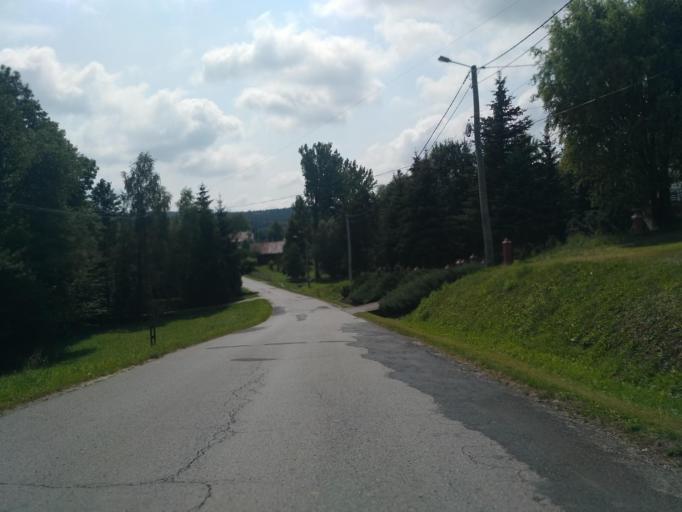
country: PL
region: Subcarpathian Voivodeship
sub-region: Powiat lancucki
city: Kraczkowa
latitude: 50.0221
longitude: 22.1795
